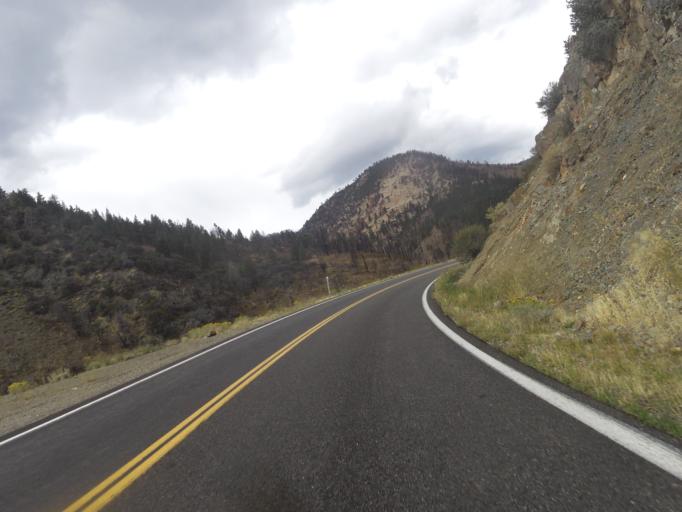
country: US
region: Nevada
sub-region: Douglas County
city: Gardnerville Ranchos
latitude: 38.6624
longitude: -119.6873
